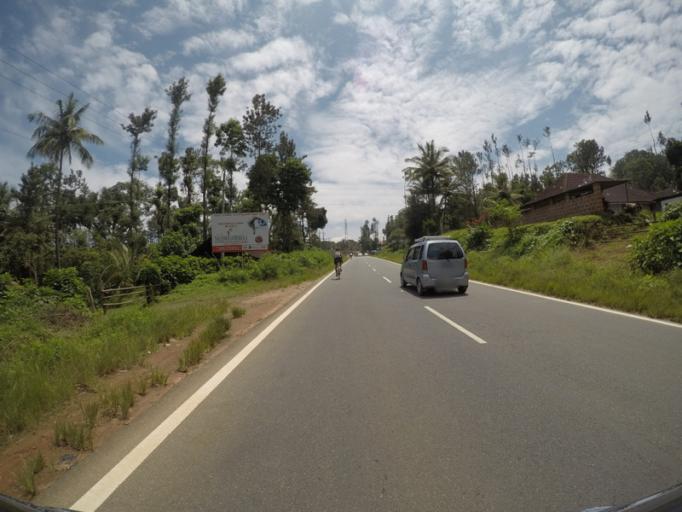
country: IN
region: Karnataka
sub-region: Kodagu
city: Suntikoppa
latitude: 12.4410
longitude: 75.8670
